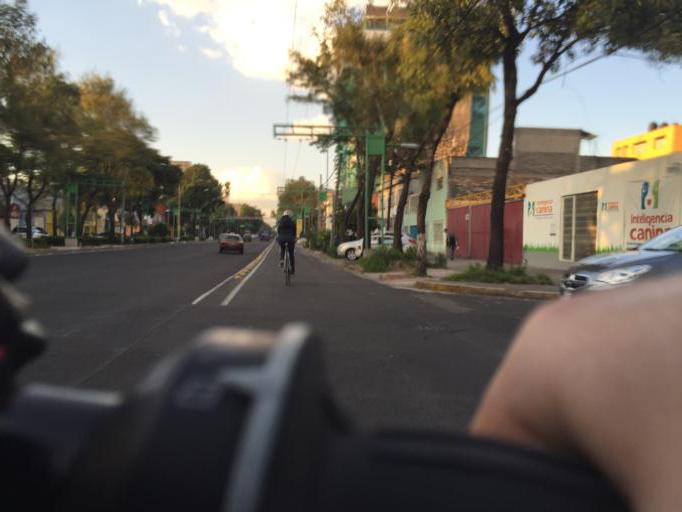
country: MX
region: Mexico City
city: Coyoacan
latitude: 19.3627
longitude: -99.1511
